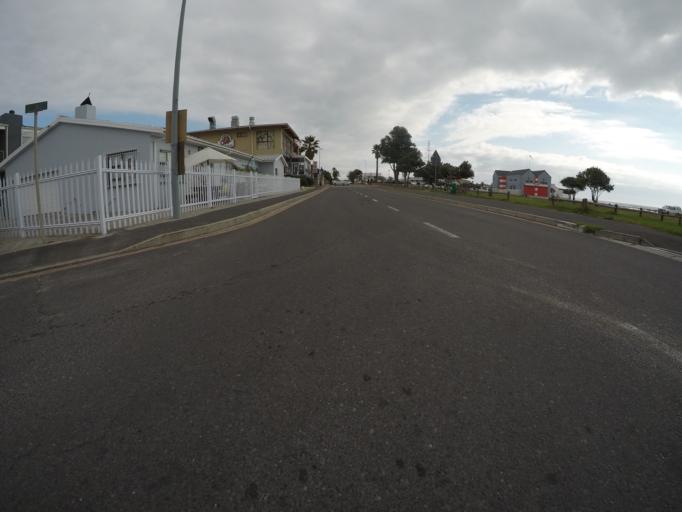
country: ZA
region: Western Cape
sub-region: City of Cape Town
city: Sunset Beach
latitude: -33.7287
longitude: 18.4397
